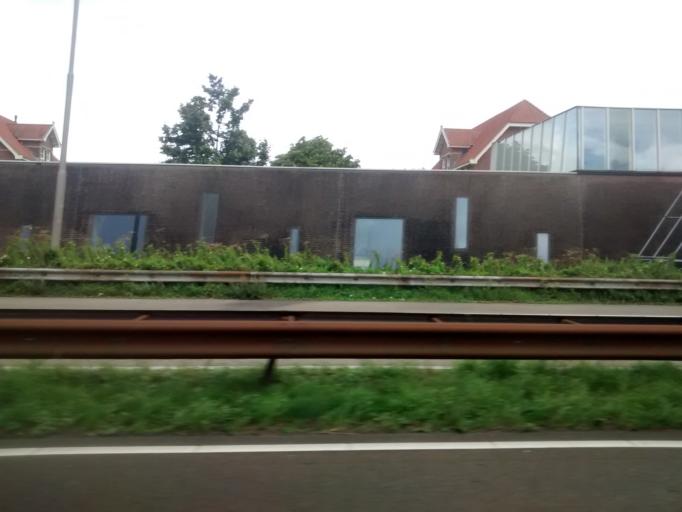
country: NL
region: Utrecht
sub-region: Gemeente Utrecht
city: Utrecht
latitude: 52.0845
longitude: 5.1471
